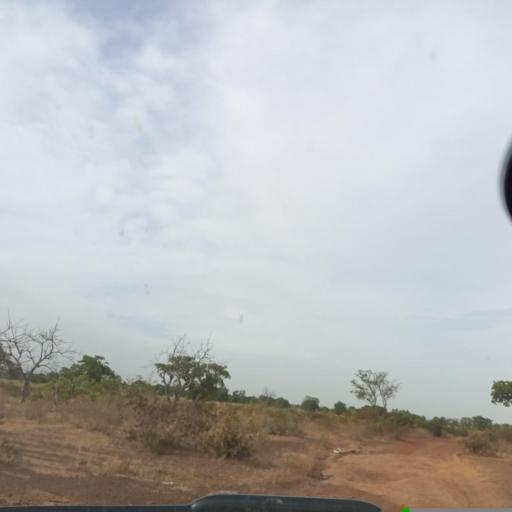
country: ML
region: Koulikoro
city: Koulikoro
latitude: 13.1094
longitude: -7.6183
